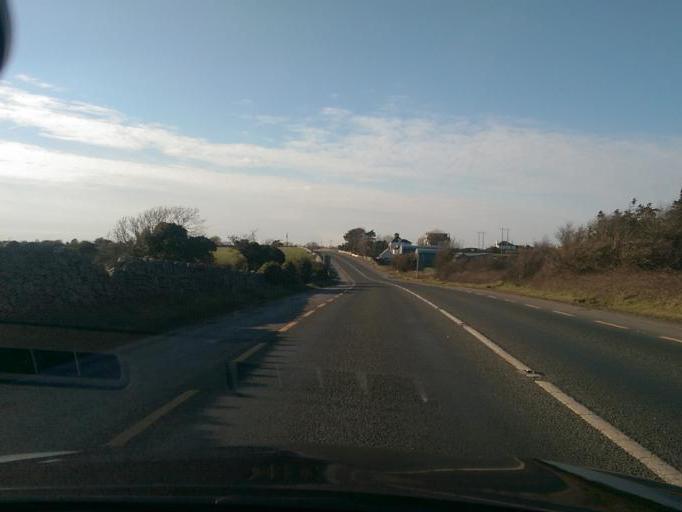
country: IE
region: Connaught
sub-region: County Galway
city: Oranmore
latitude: 53.2522
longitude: -8.9052
